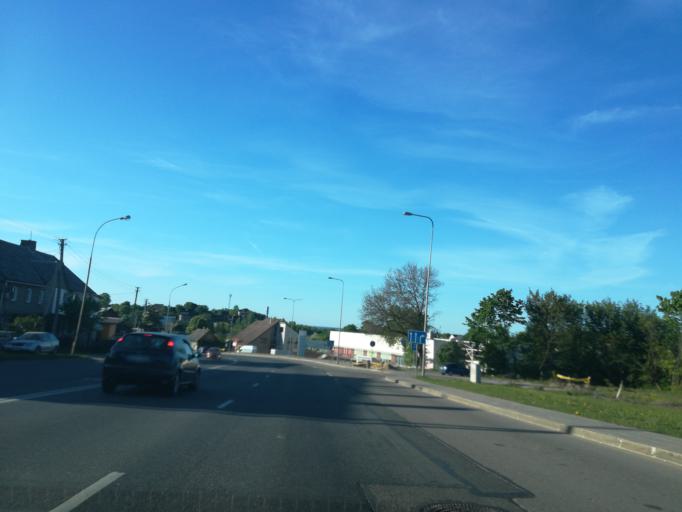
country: LT
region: Vilnius County
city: Rasos
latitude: 54.6597
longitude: 25.3035
